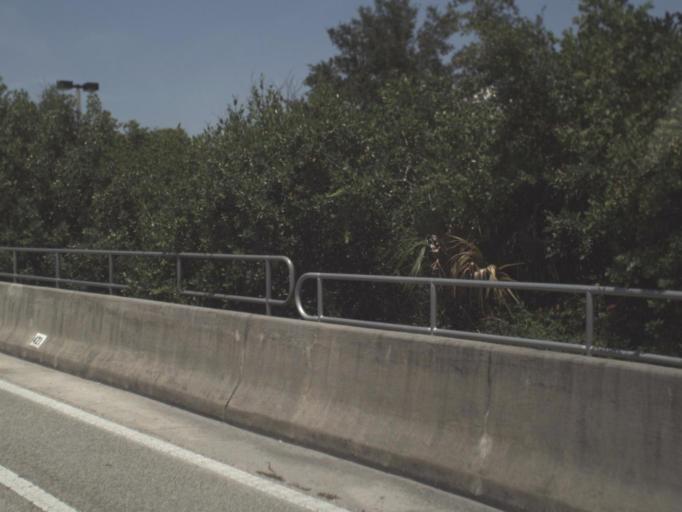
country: US
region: Florida
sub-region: Hillsborough County
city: Ruskin
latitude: 27.7189
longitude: -82.4340
